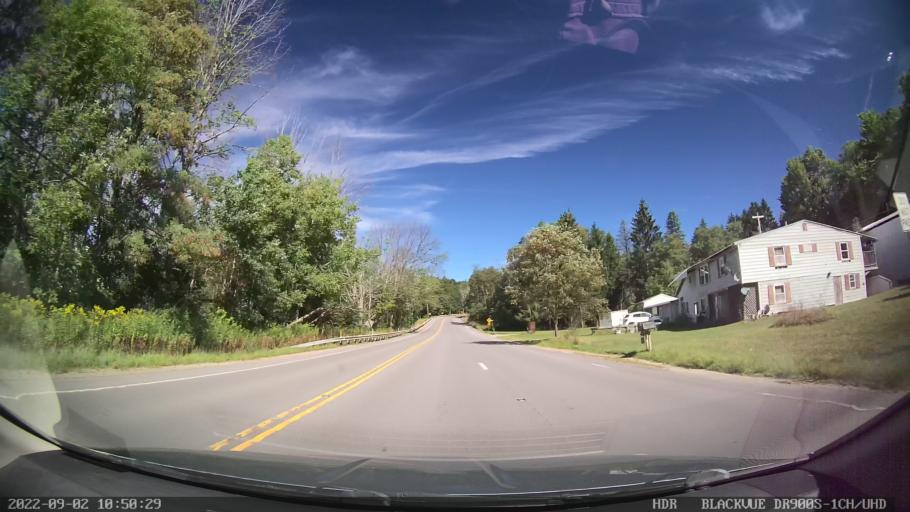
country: US
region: Pennsylvania
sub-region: Tioga County
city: Blossburg
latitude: 41.6147
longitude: -77.1183
